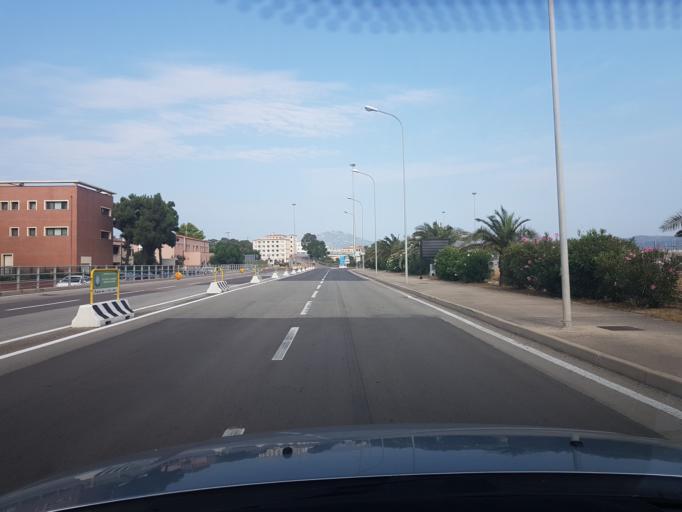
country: IT
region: Sardinia
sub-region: Provincia di Olbia-Tempio
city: Olbia
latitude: 40.9246
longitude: 9.5115
